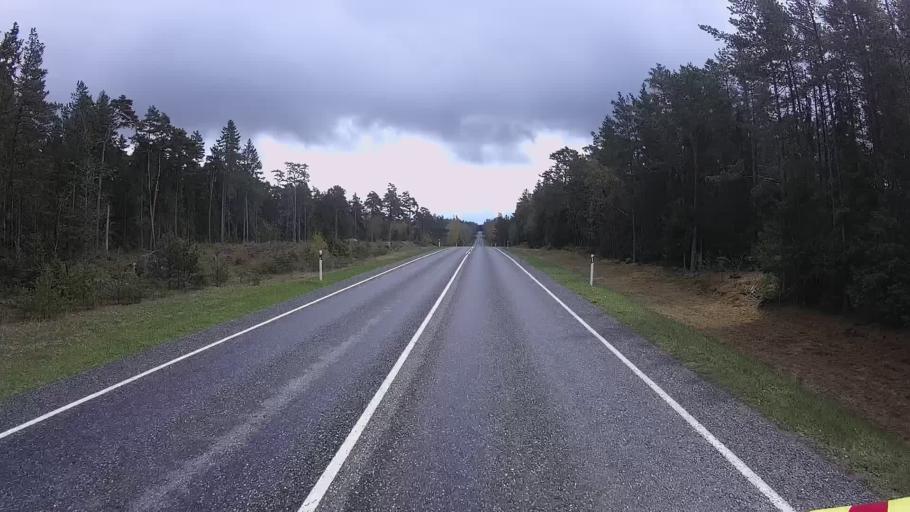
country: EE
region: Hiiumaa
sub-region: Kaerdla linn
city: Kardla
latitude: 58.9598
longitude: 22.8528
